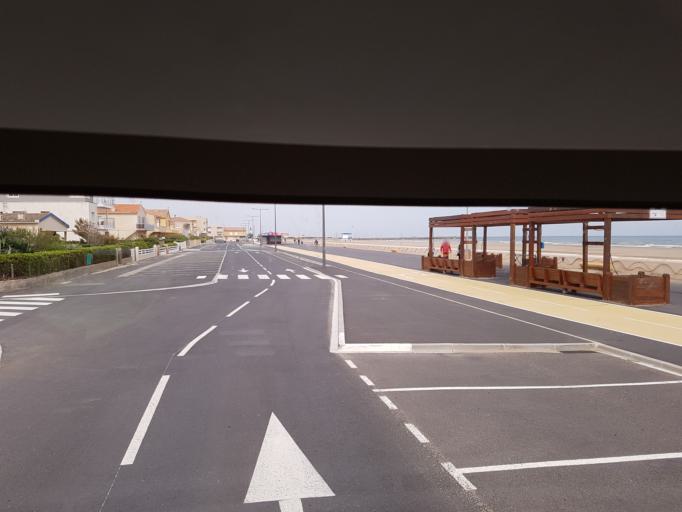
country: FR
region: Languedoc-Roussillon
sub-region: Departement de l'Aude
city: Fleury
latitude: 43.1647
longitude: 3.1742
